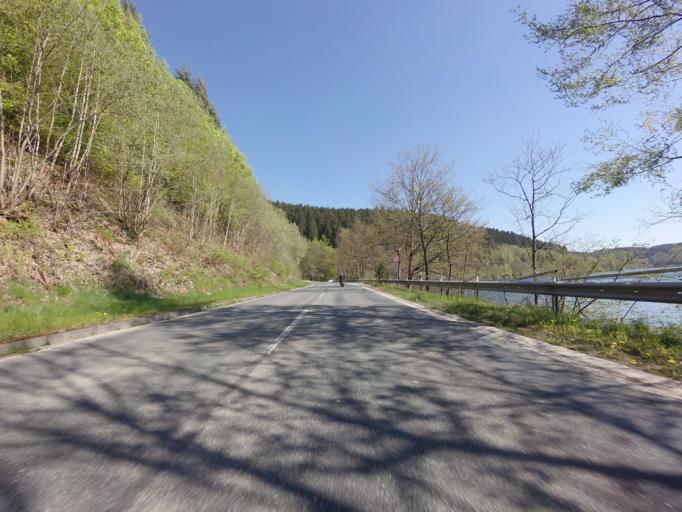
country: DE
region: North Rhine-Westphalia
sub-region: Regierungsbezirk Arnsberg
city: Olpe
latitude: 51.0898
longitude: 7.8241
